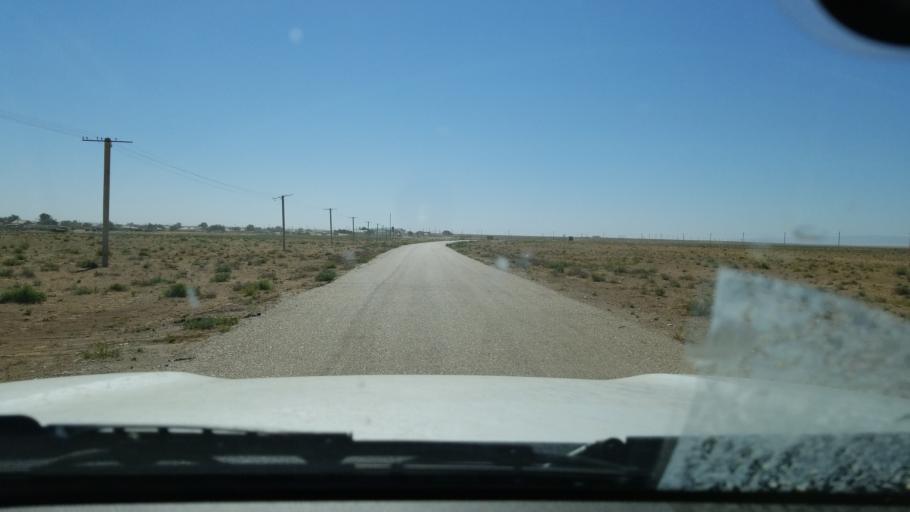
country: TM
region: Balkan
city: Balkanabat
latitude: 40.1564
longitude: 54.3460
